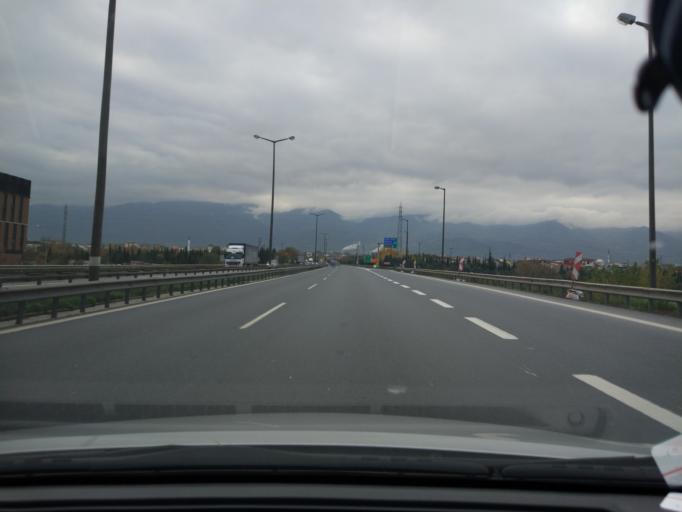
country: TR
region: Kocaeli
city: Kosekoy
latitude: 40.7501
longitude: 30.0400
